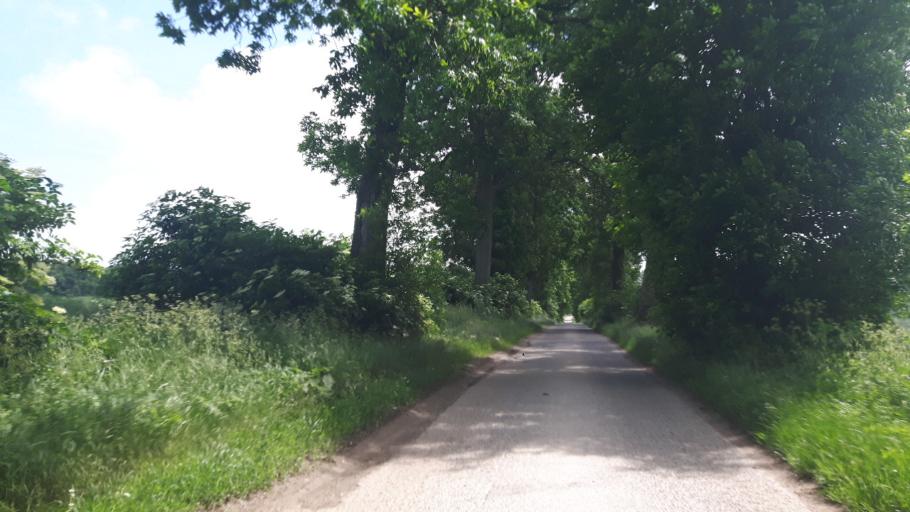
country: PL
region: West Pomeranian Voivodeship
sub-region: Powiat slawienski
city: Darlowo
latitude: 54.4694
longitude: 16.4833
